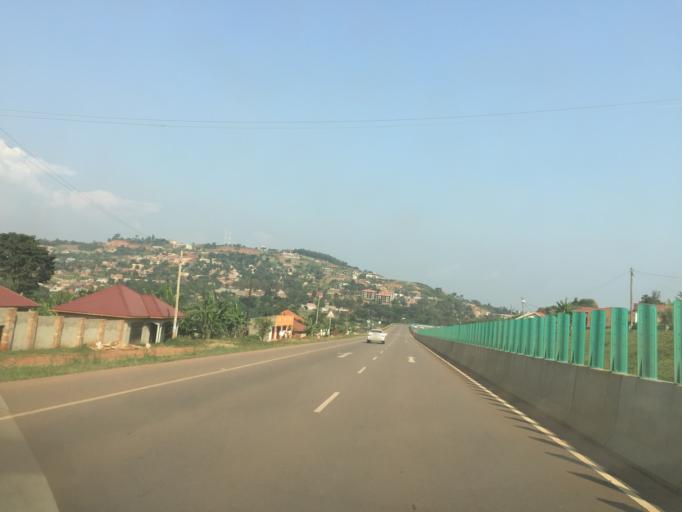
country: UG
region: Central Region
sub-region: Wakiso District
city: Kajansi
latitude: 0.2107
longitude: 32.5792
